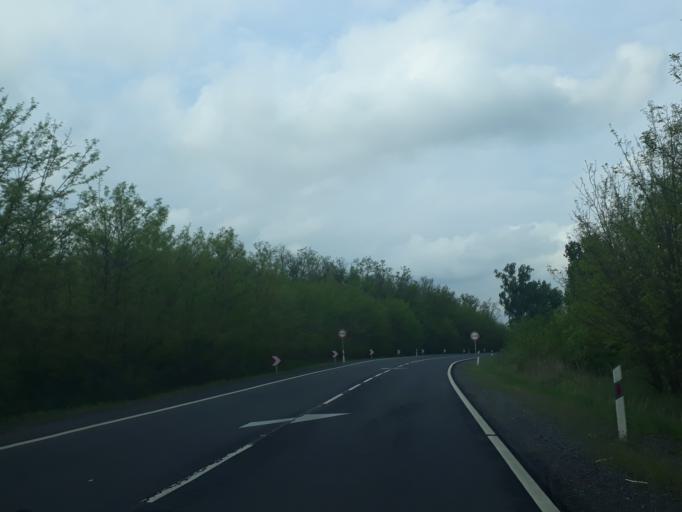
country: HU
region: Szabolcs-Szatmar-Bereg
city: Nyirtass
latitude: 48.1143
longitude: 21.9912
